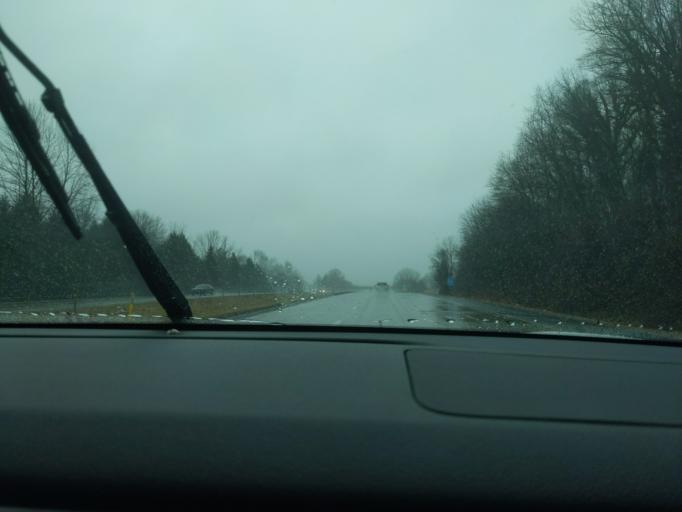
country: US
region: Pennsylvania
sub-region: Bucks County
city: Doylestown
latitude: 40.3254
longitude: -75.1398
